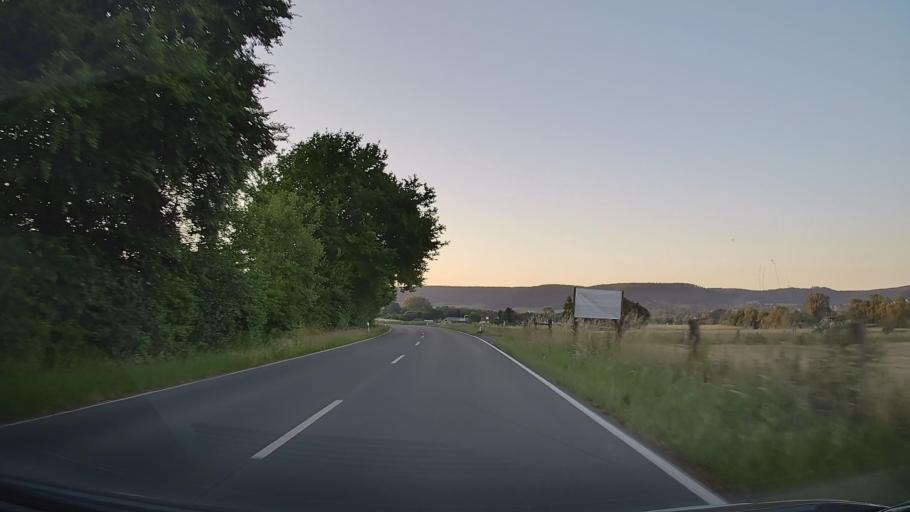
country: DE
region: North Rhine-Westphalia
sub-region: Regierungsbezirk Detmold
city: Lugde
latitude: 51.9687
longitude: 9.2352
